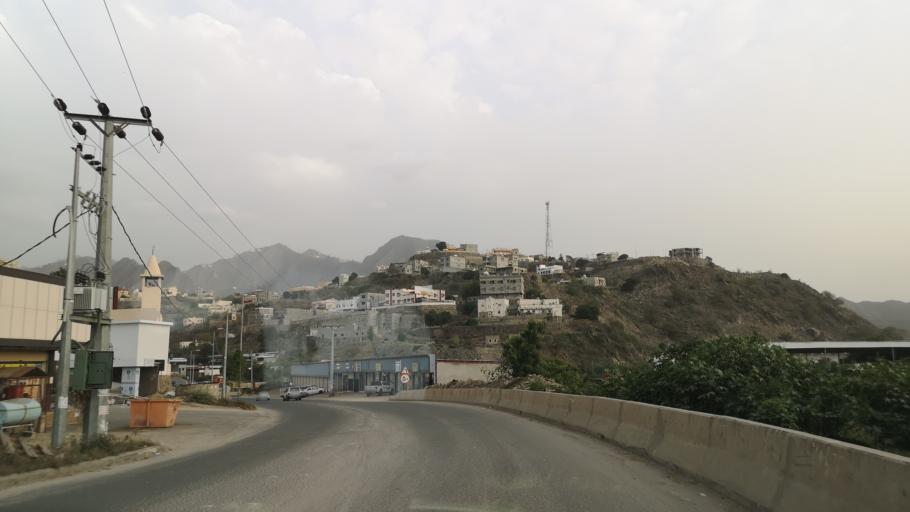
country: YE
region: Sa'dah
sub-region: Monabbih
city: Suq al Khamis
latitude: 17.3506
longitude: 43.1358
